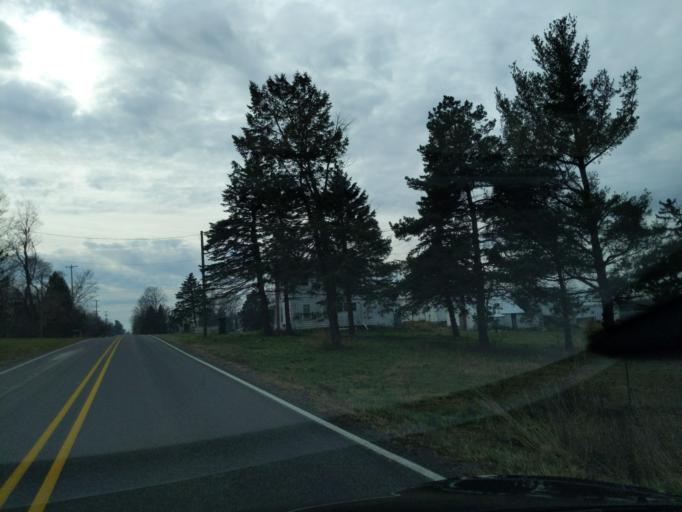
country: US
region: Michigan
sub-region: Ingham County
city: Mason
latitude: 42.5189
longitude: -84.5223
